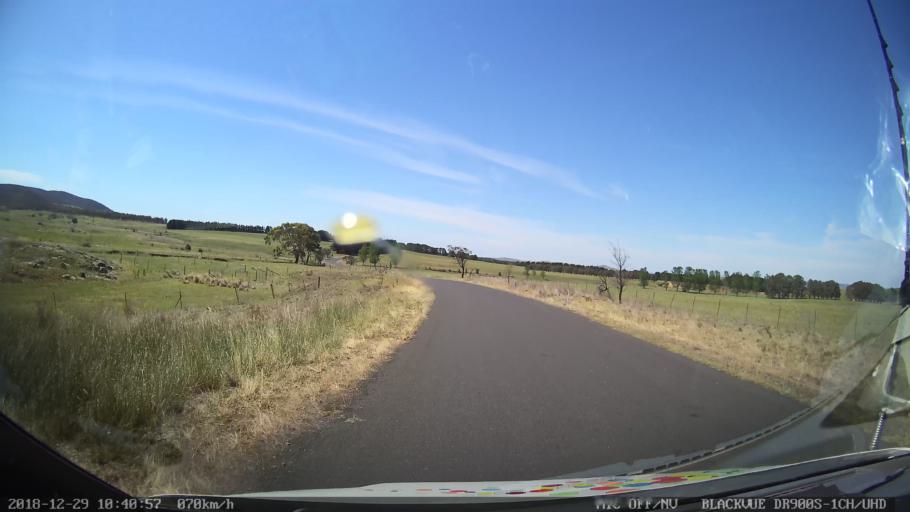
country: AU
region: New South Wales
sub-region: Palerang
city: Bungendore
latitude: -35.0202
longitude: 149.5195
